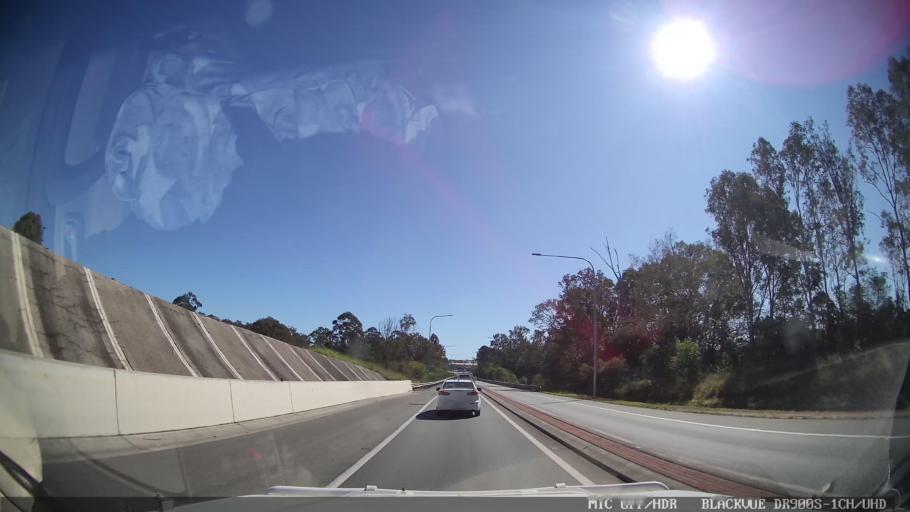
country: AU
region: Queensland
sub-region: Gympie Regional Council
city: Monkland
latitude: -26.2350
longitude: 152.6986
